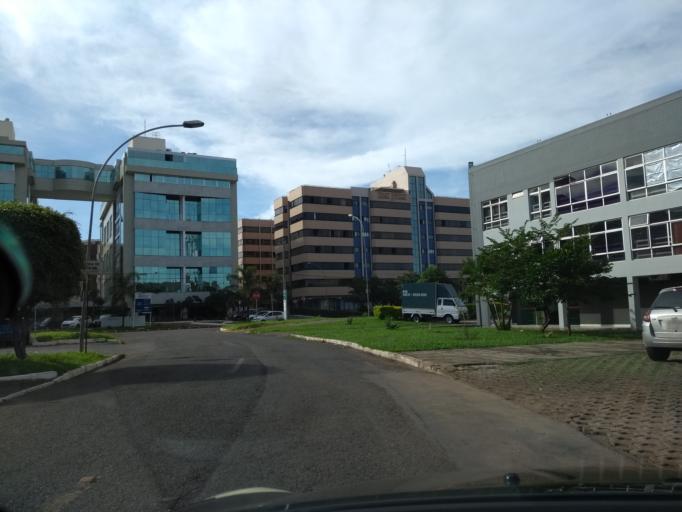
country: BR
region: Federal District
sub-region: Brasilia
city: Brasilia
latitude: -15.7952
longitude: -47.9292
